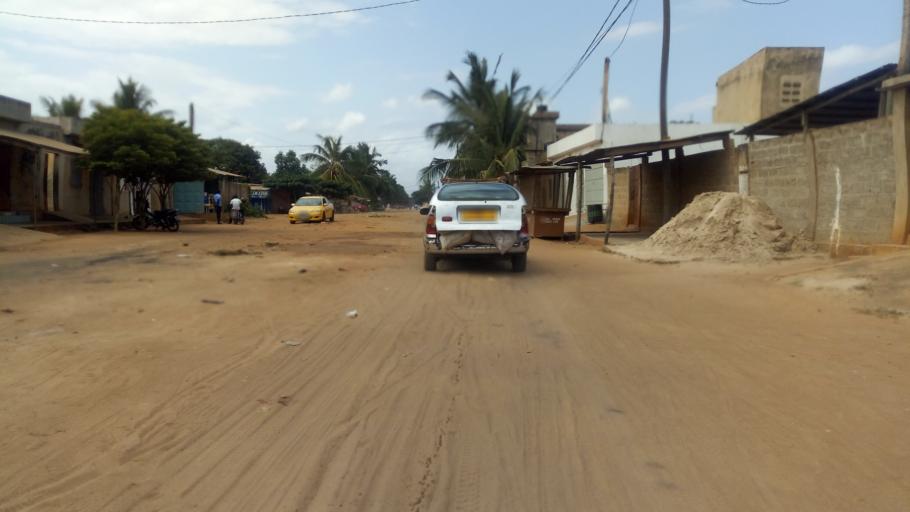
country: TG
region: Maritime
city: Lome
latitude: 6.2253
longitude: 1.1789
